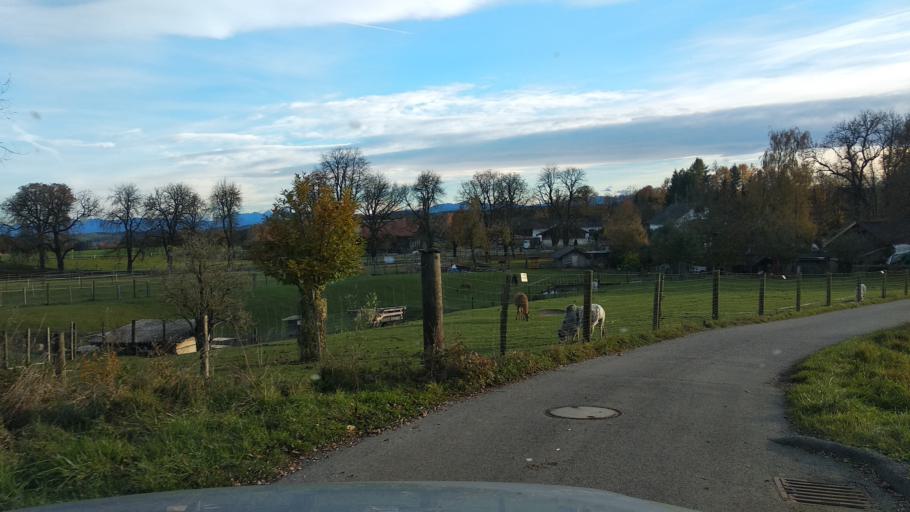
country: DE
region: Bavaria
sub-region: Upper Bavaria
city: Moosach
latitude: 48.0380
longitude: 11.8898
